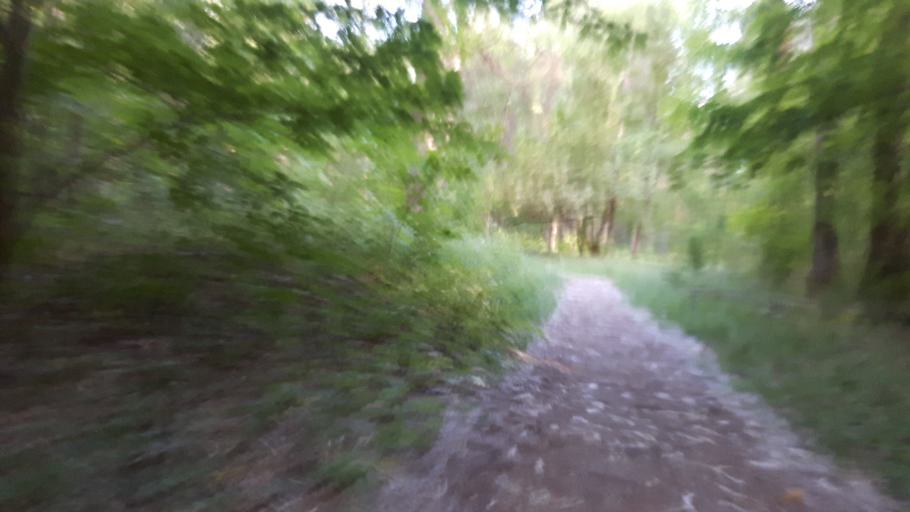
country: LV
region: Riga
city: Jaunciems
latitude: 57.0152
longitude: 24.1337
